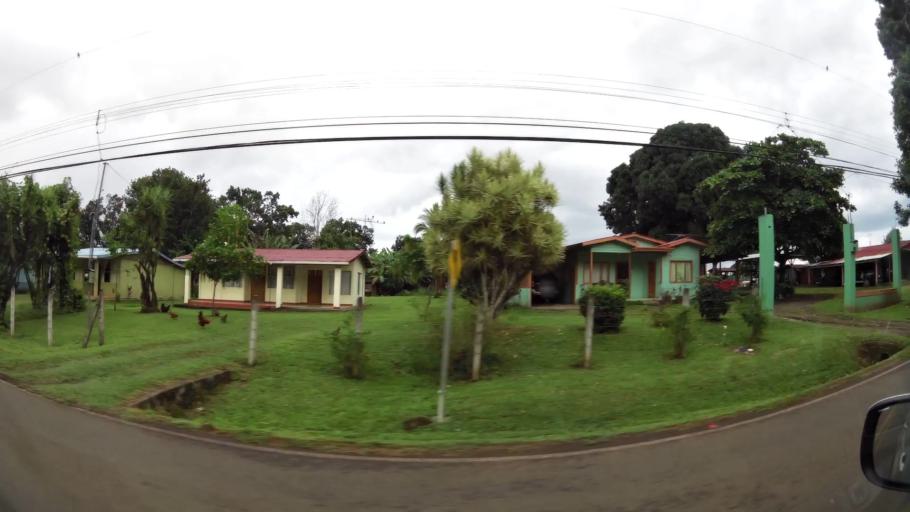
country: CR
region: Puntarenas
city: Esparza
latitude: 9.9657
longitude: -84.6144
